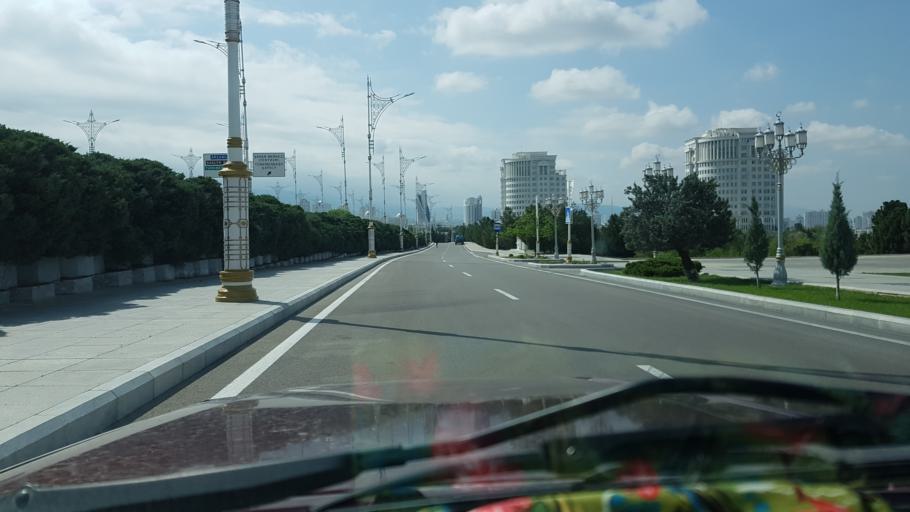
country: TM
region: Ahal
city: Ashgabat
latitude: 37.8795
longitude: 58.3819
